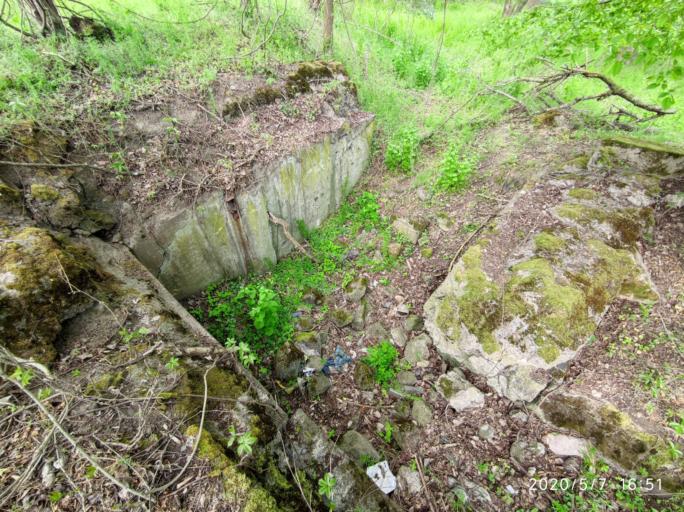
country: PL
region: Lubusz
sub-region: Powiat zielonogorski
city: Sulechow
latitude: 52.0288
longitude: 15.6071
